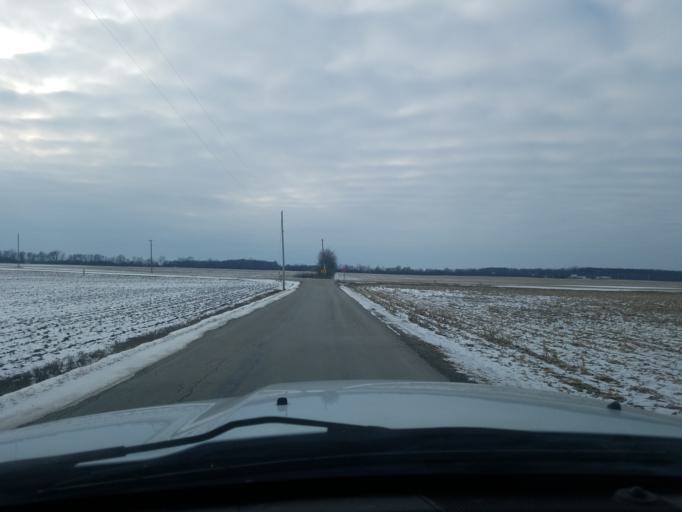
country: US
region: Indiana
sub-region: Randolph County
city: Winchester
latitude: 40.1975
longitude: -84.9776
